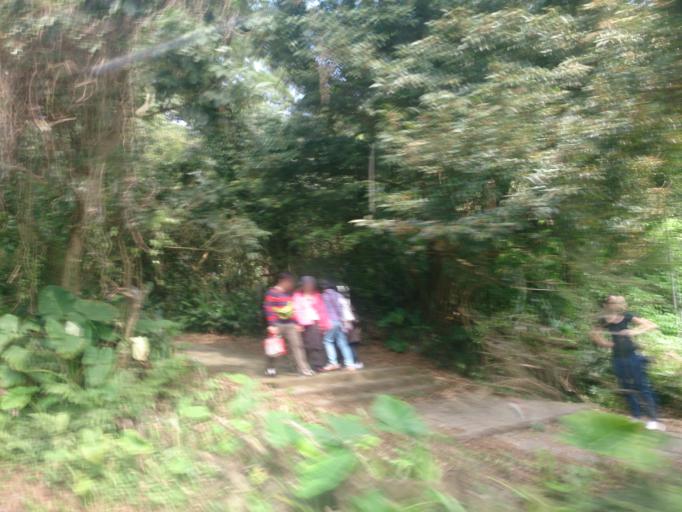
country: TW
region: Taipei
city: Taipei
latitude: 25.1572
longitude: 121.5467
